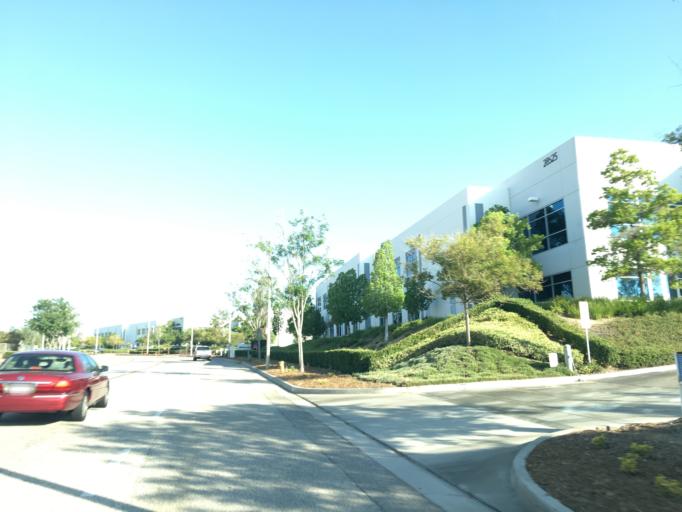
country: US
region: California
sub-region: Los Angeles County
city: Valencia
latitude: 34.4523
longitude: -118.6324
